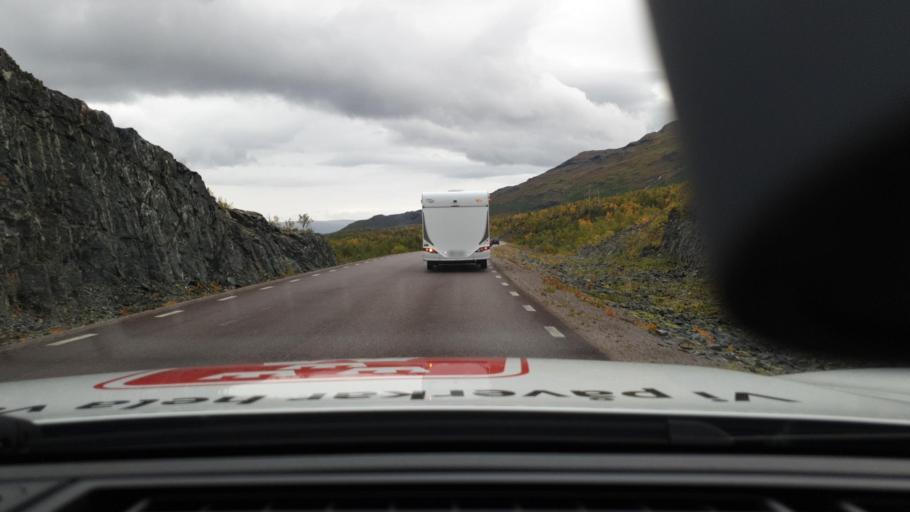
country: NO
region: Troms
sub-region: Bardu
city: Setermoen
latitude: 68.4301
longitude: 18.4632
